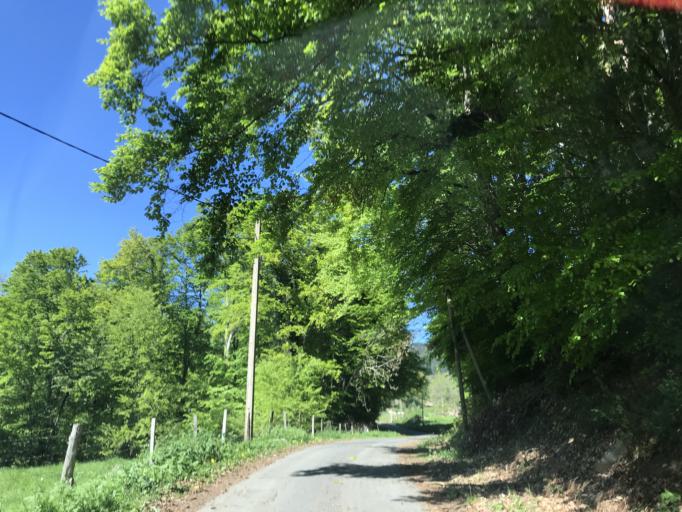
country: FR
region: Auvergne
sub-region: Departement du Puy-de-Dome
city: Escoutoux
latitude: 45.7822
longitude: 3.6179
